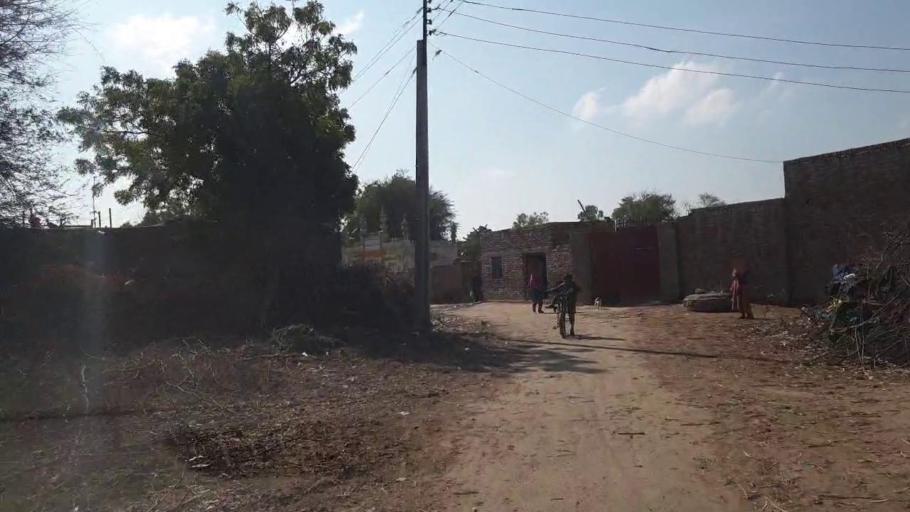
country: PK
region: Sindh
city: Shahpur Chakar
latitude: 26.0521
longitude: 68.5839
